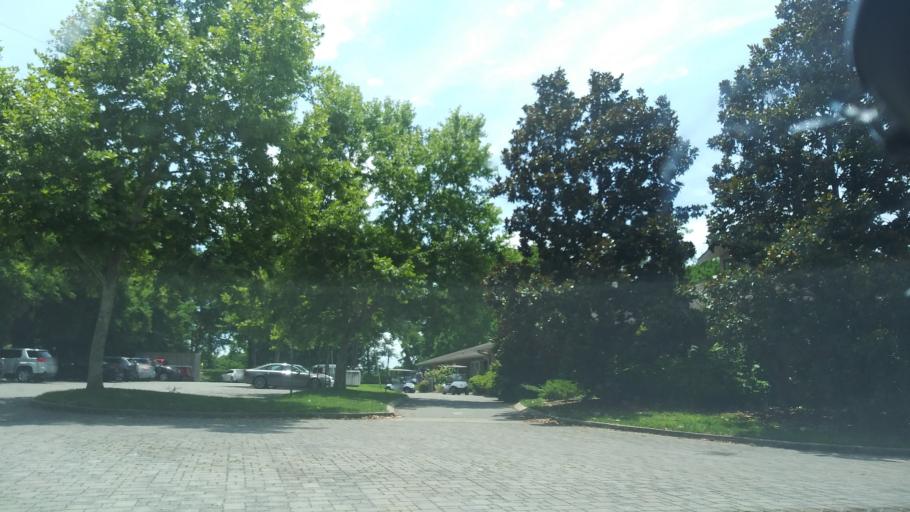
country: US
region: Tennessee
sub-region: Davidson County
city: Belle Meade
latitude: 36.1403
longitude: -86.8424
